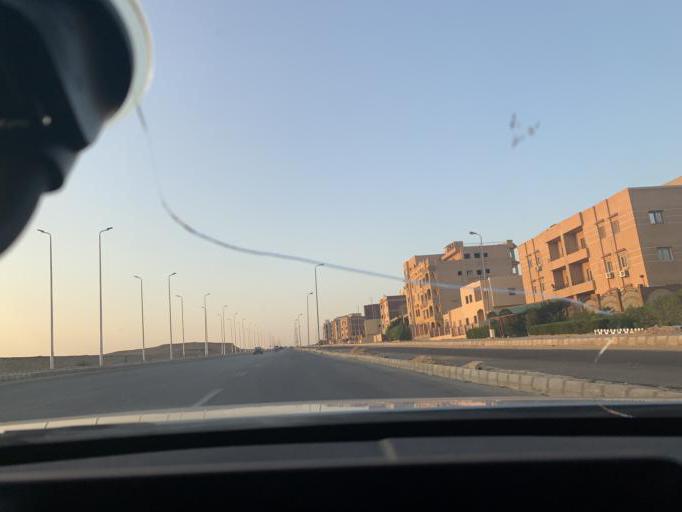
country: EG
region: Muhafazat al Qahirah
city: Halwan
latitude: 29.9791
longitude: 31.4689
